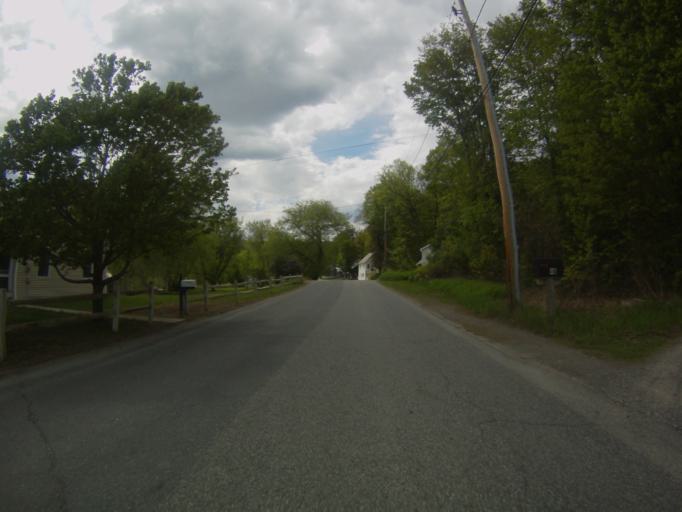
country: US
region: New York
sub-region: Essex County
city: Ticonderoga
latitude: 43.8824
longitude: -73.4516
